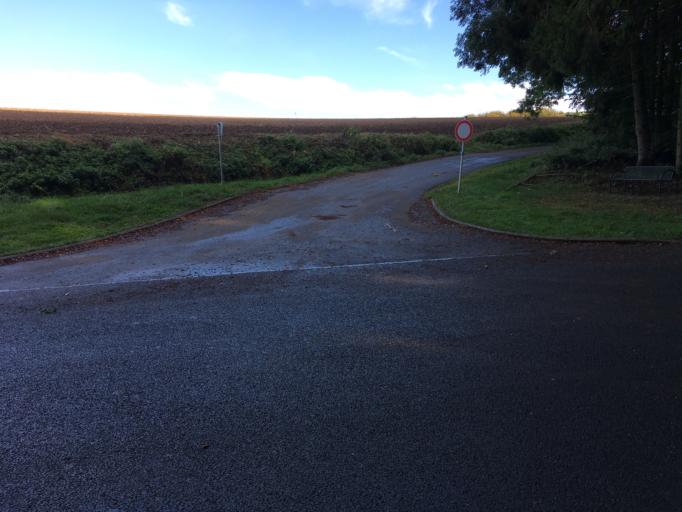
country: LU
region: Diekirch
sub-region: Canton de Diekirch
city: Niederfeulen
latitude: 49.8402
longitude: 6.0385
